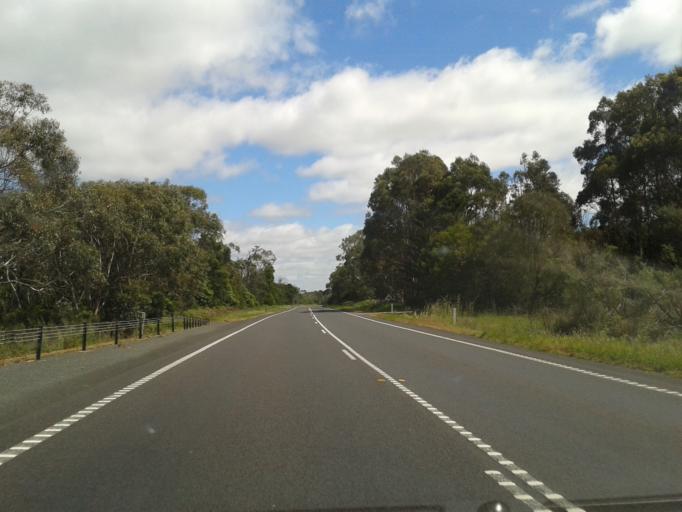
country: AU
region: Victoria
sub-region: Glenelg
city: Portland
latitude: -38.2264
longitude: 141.8244
